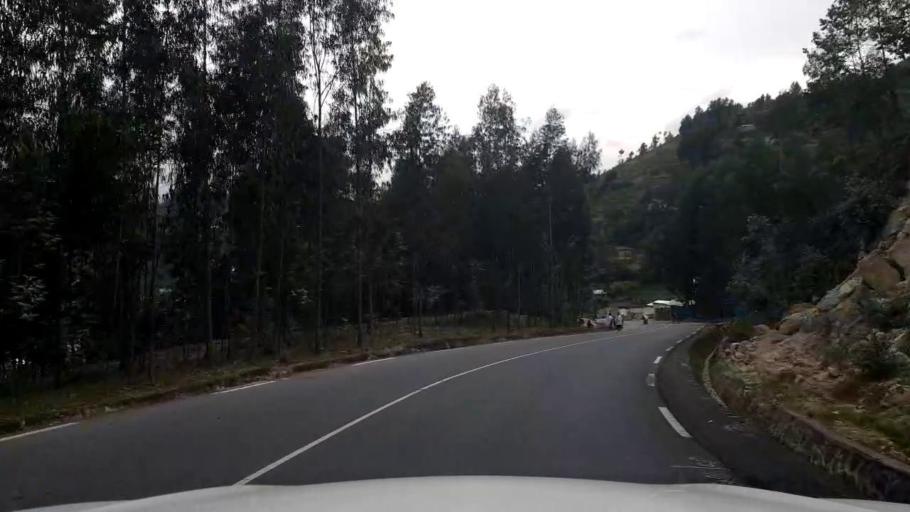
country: RW
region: Northern Province
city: Musanze
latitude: -1.6808
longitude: 29.5168
